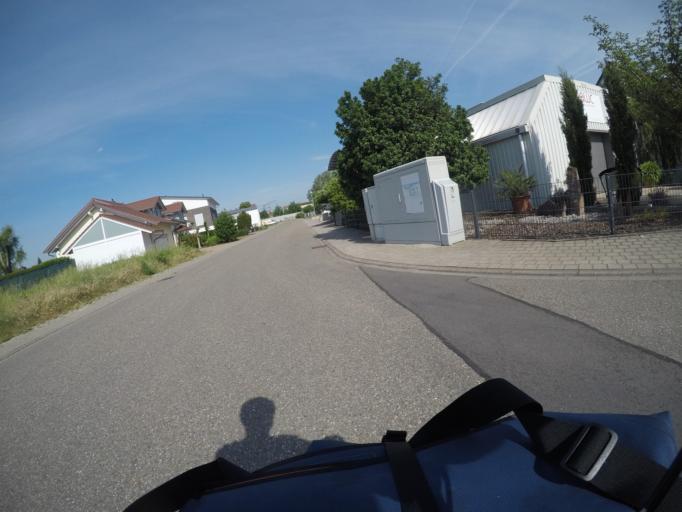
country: DE
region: Baden-Wuerttemberg
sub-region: Karlsruhe Region
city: Bietigheim
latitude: 48.9080
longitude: 8.2582
